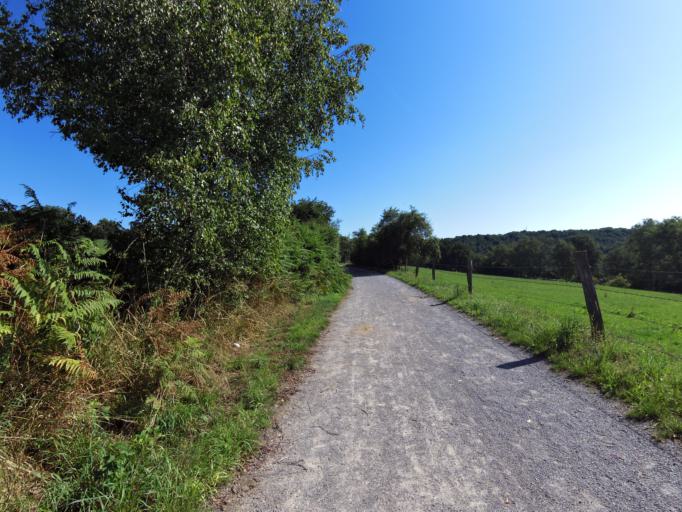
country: DE
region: North Rhine-Westphalia
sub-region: Regierungsbezirk Koln
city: Wurselen
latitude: 50.8088
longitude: 6.1007
